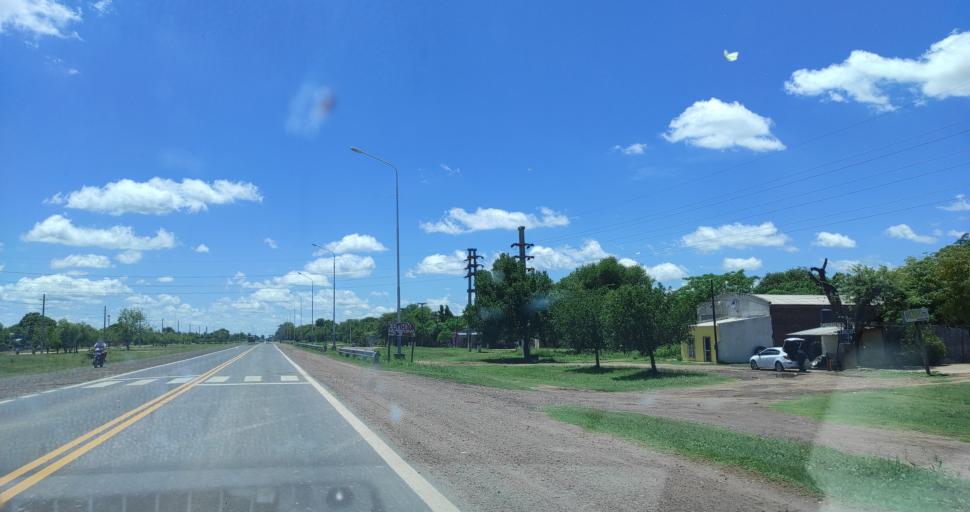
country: AR
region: Chaco
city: Campo Largo
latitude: -26.8098
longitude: -60.8403
